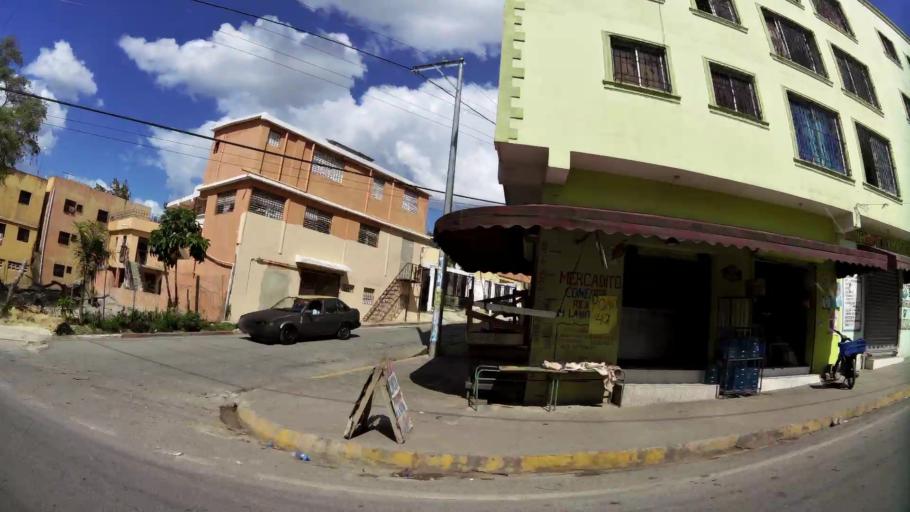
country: DO
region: Nacional
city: Ensanche Luperon
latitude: 18.5364
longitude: -69.8988
